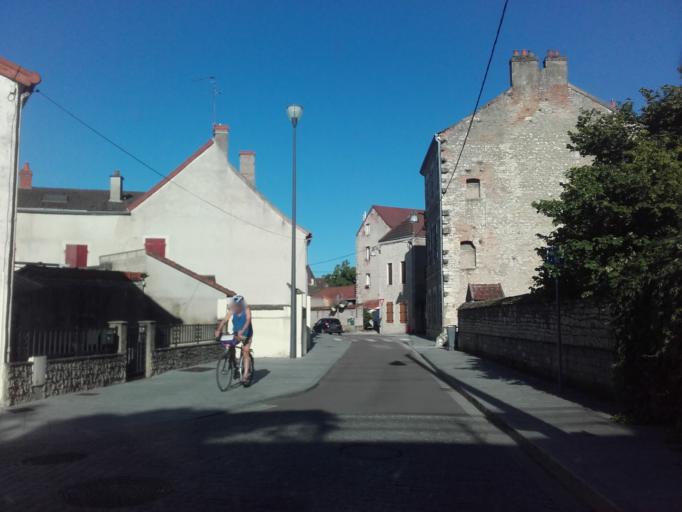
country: FR
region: Bourgogne
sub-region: Departement de Saone-et-Loire
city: Chagny
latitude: 46.9115
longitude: 4.7487
